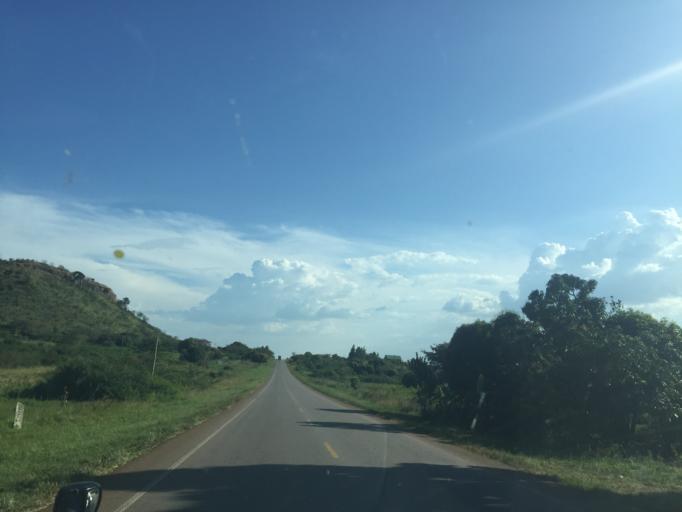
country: UG
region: Central Region
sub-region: Nakasongola District
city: Nakasongola
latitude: 1.3165
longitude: 32.4221
